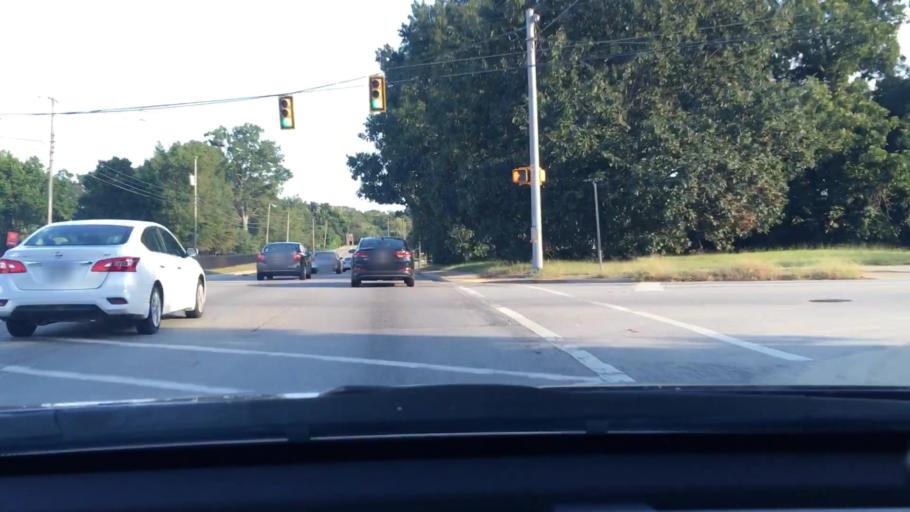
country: US
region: South Carolina
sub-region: Sumter County
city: South Sumter
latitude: 33.9156
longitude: -80.3566
